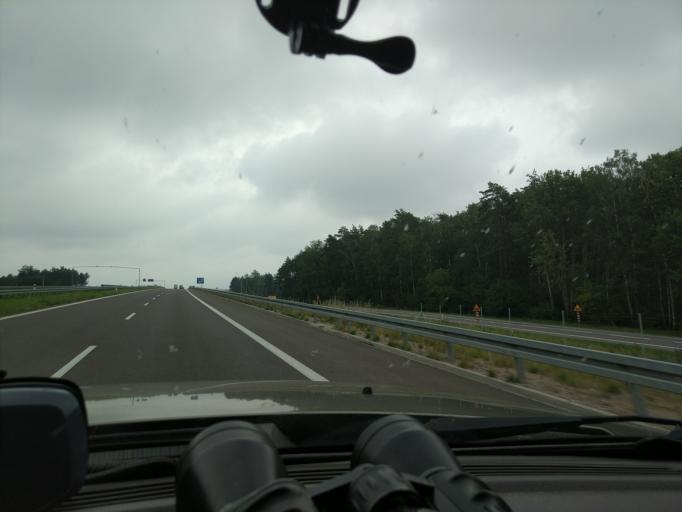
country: PL
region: Podlasie
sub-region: Powiat zambrowski
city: Rutki-Kossaki
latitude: 53.0440
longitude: 22.3659
